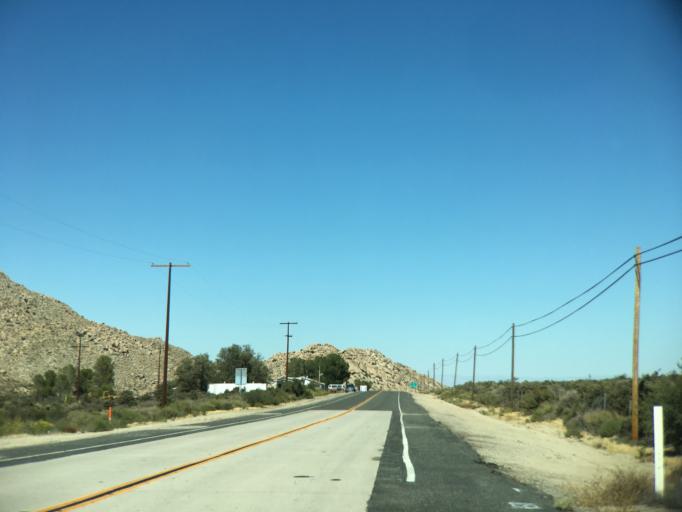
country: MX
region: Baja California
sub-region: Tecate
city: Cereso del Hongo
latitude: 32.6431
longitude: -116.1077
